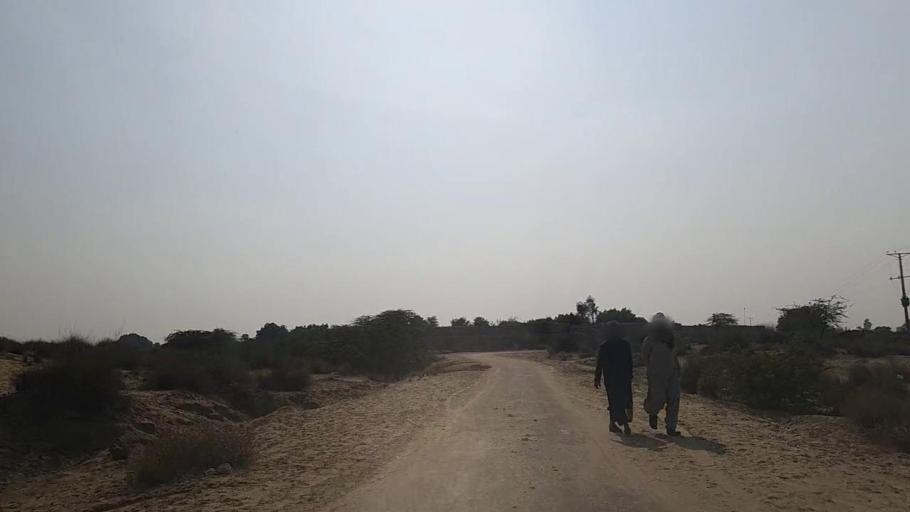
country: PK
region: Sindh
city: Daur
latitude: 26.4638
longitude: 68.4673
